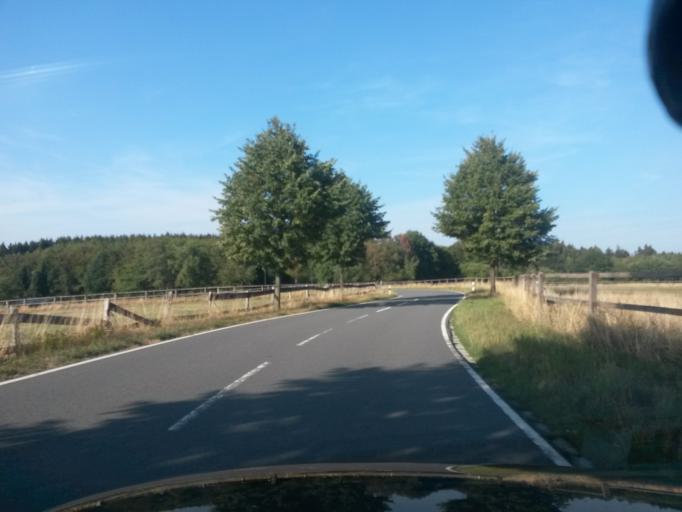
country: DE
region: North Rhine-Westphalia
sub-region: Regierungsbezirk Koln
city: Numbrecht
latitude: 50.8935
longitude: 7.5156
